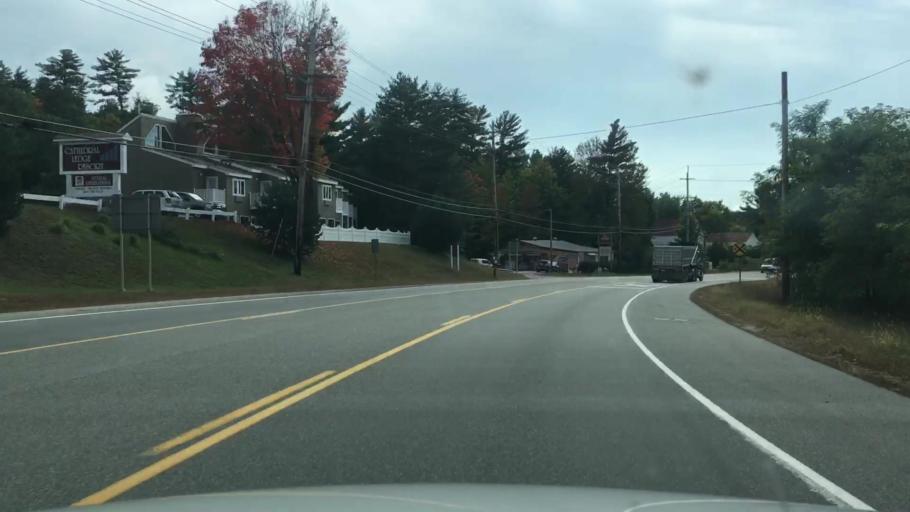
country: US
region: New Hampshire
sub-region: Carroll County
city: North Conway
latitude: 44.0776
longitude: -71.1390
